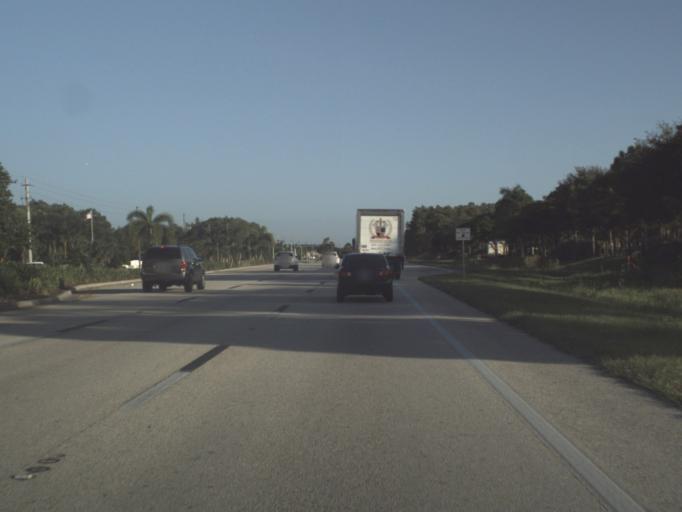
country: US
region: Florida
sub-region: Lee County
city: Estero
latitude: 26.4060
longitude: -81.8110
